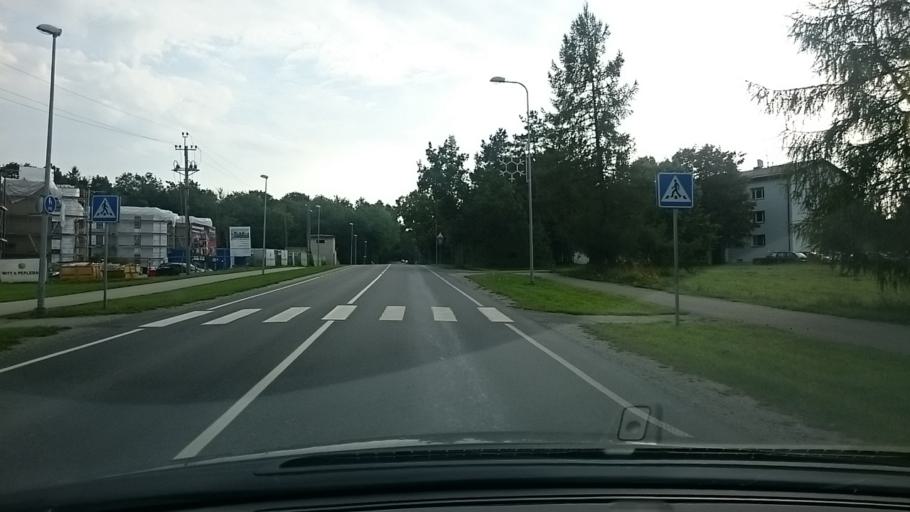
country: EE
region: Harju
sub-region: Saue vald
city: Laagri
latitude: 59.3885
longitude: 24.5789
